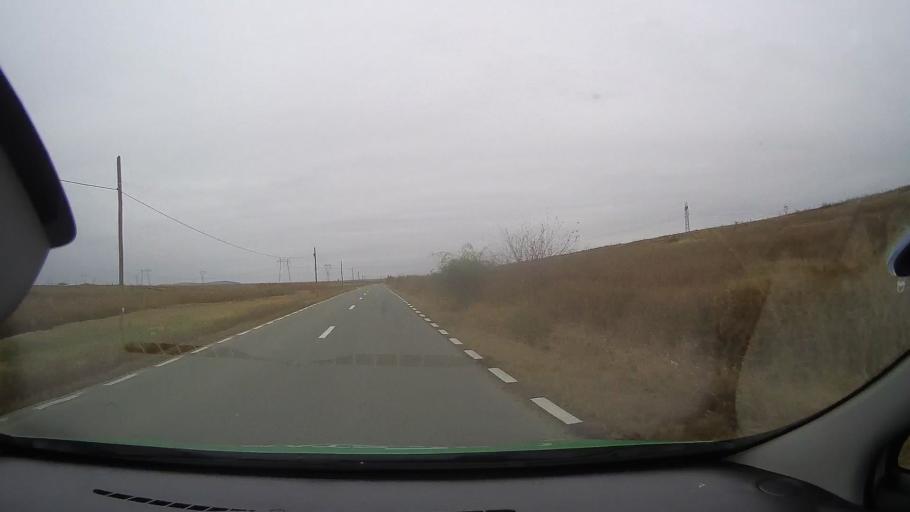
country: RO
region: Constanta
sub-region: Comuna Silistea
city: Silistea
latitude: 44.4321
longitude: 28.2183
